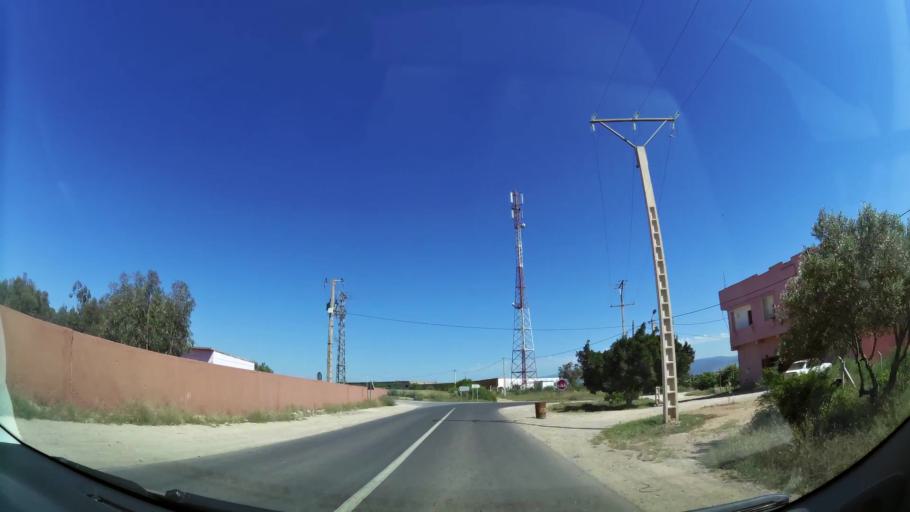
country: MA
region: Oriental
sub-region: Berkane-Taourirt
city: Madagh
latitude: 35.0122
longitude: -2.3978
